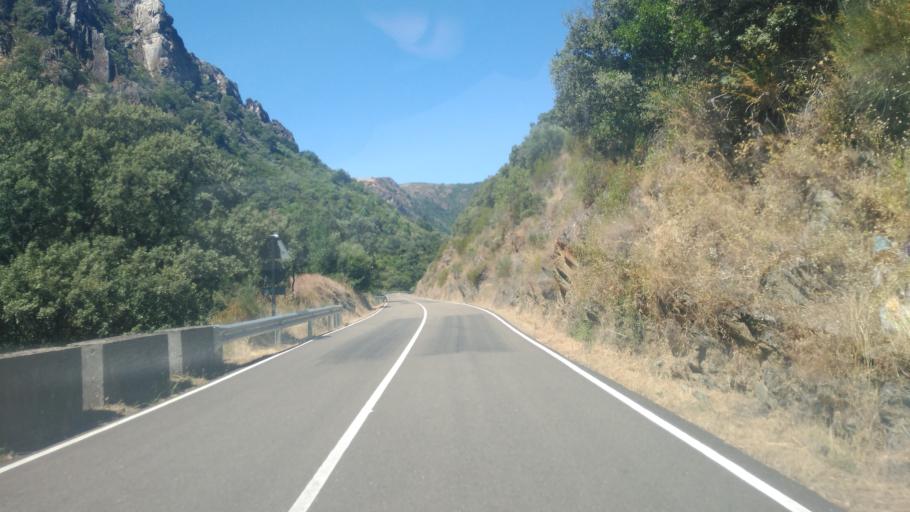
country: ES
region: Castille and Leon
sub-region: Provincia de Salamanca
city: Mieza
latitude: 41.1868
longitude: -6.6745
